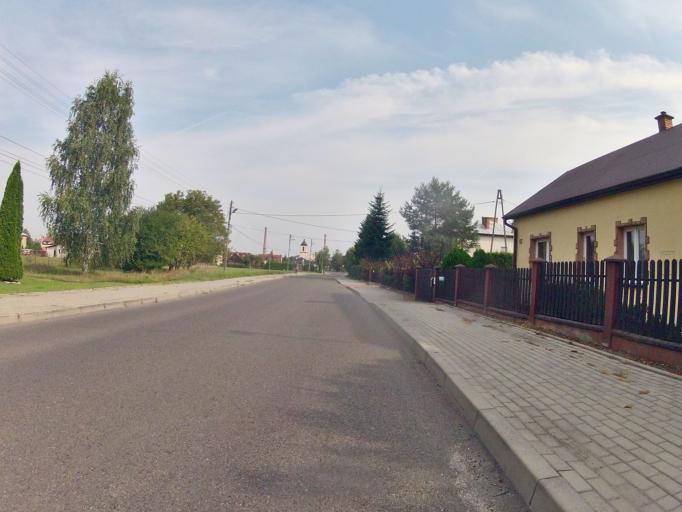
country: PL
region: Subcarpathian Voivodeship
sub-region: Powiat jasielski
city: Debowiec
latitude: 49.7152
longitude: 21.4616
